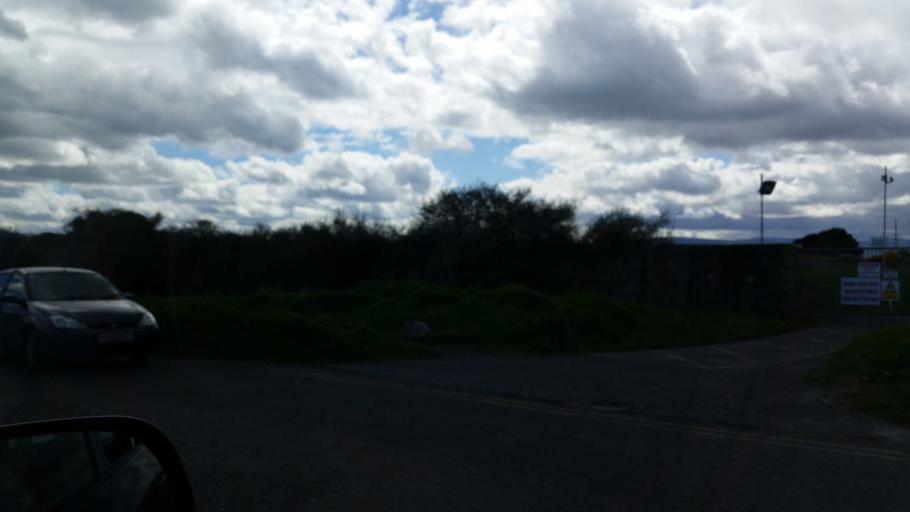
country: IE
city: Bayside
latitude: 53.3706
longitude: -6.1498
